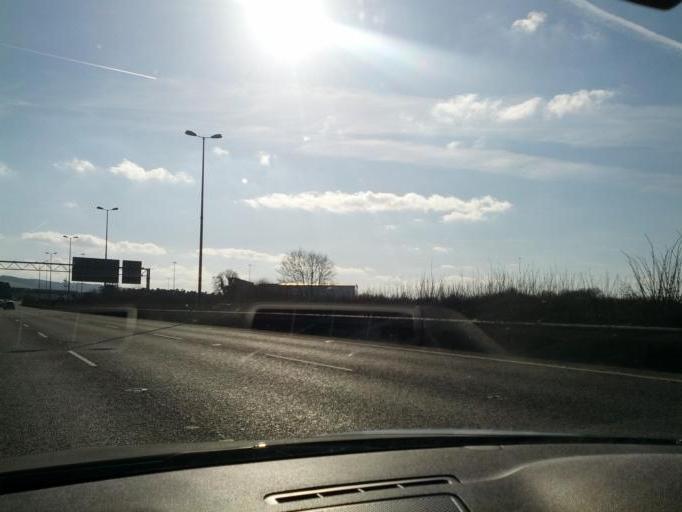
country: IE
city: Jobstown
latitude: 53.2973
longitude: -6.4250
